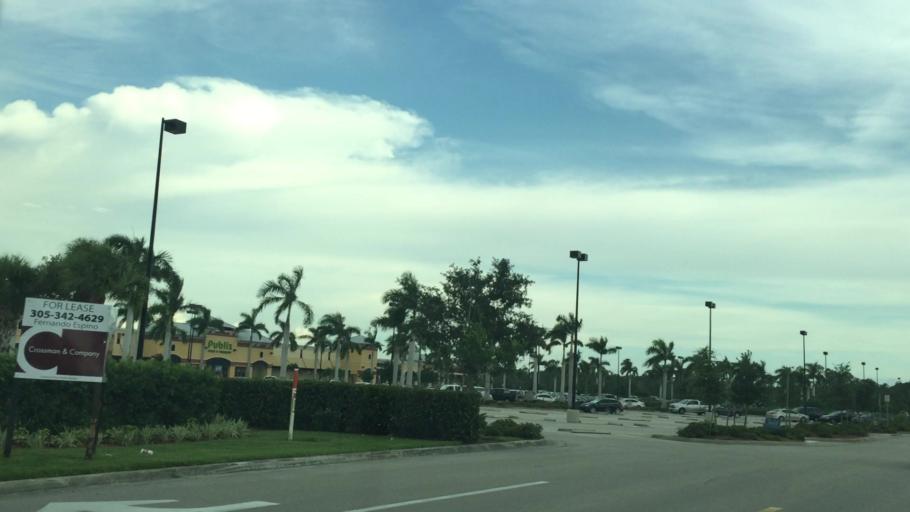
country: US
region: Florida
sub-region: Lee County
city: Fort Myers
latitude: 26.6051
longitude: -81.8101
